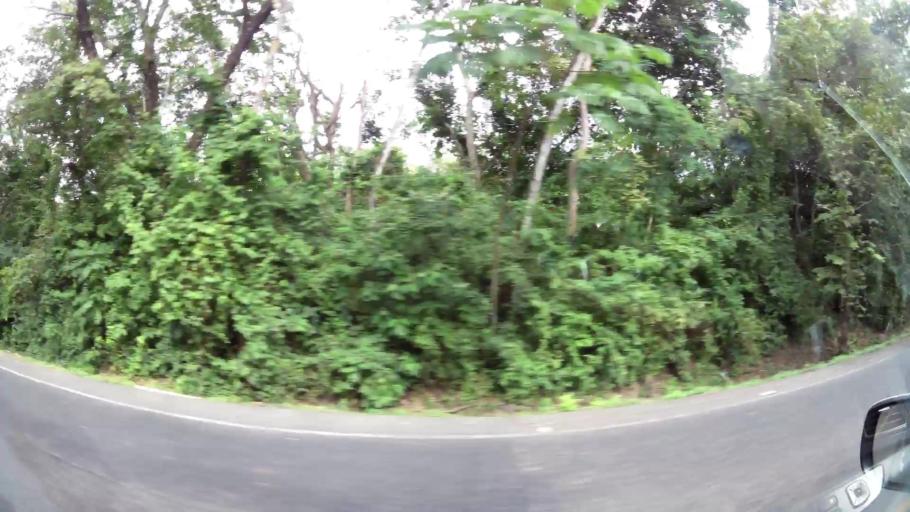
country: CR
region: Guanacaste
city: Juntas
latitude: 10.1549
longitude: -84.9145
